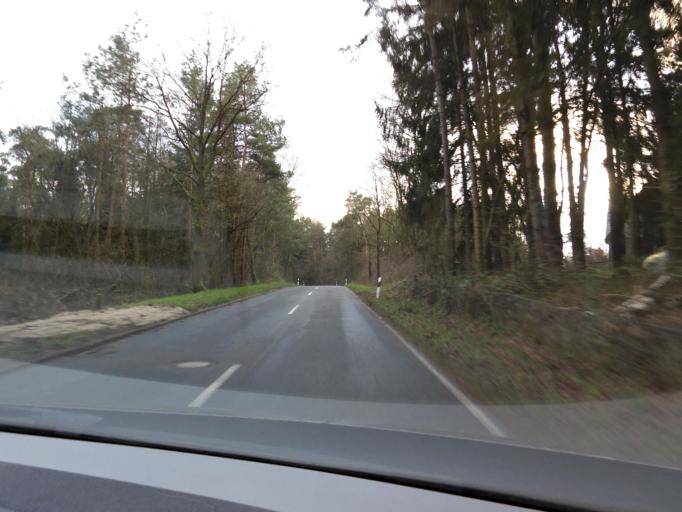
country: DE
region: Schleswig-Holstein
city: Seedorf
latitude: 53.6398
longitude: 10.8577
